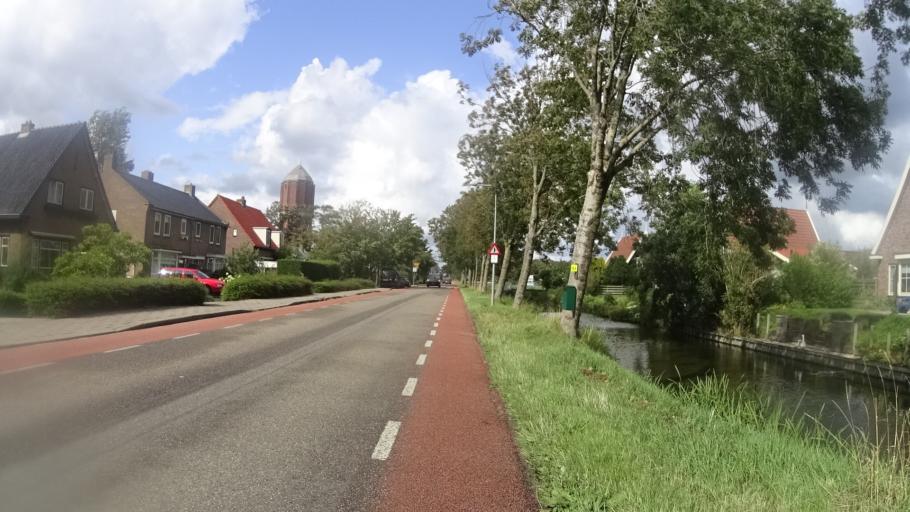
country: NL
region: North Holland
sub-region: Gemeente Schagen
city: Schagen
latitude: 52.8384
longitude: 4.8608
